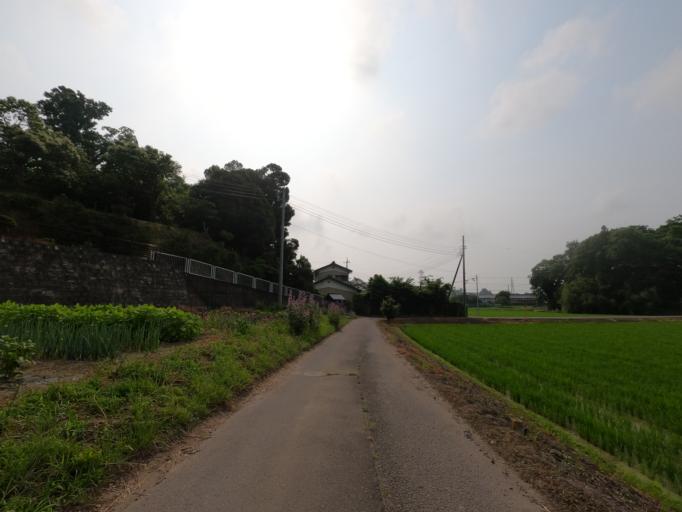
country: JP
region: Ibaraki
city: Moriya
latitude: 35.9590
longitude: 139.9499
